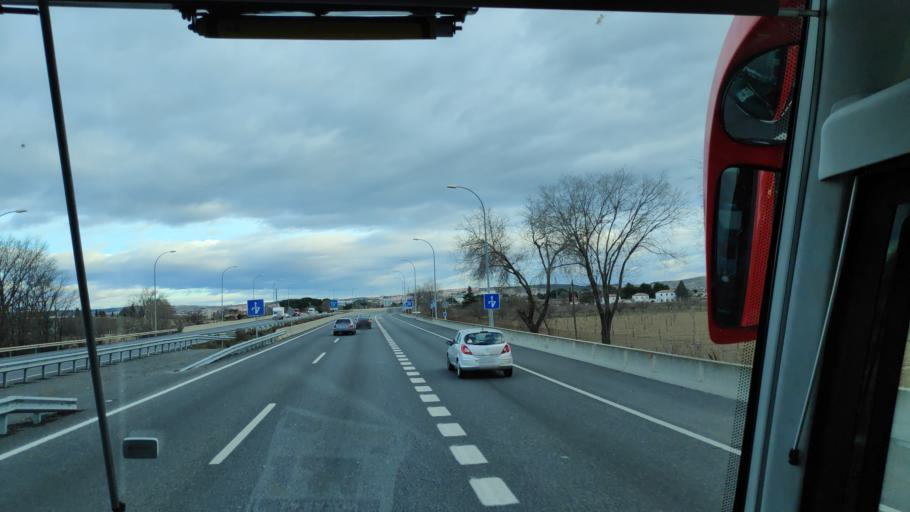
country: ES
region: Madrid
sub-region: Provincia de Madrid
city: Vaciamadrid
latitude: 40.3148
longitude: -3.5009
